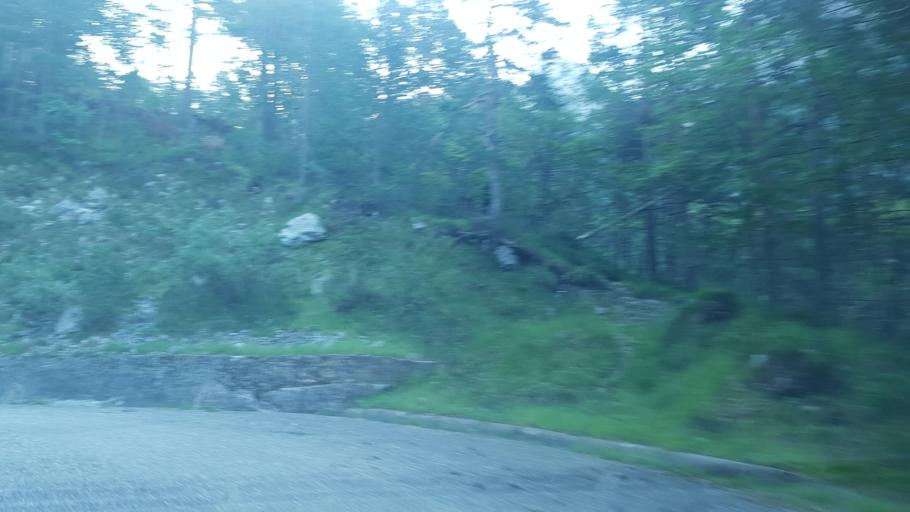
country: IT
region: Friuli Venezia Giulia
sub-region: Provincia di Udine
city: Malborghetto
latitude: 46.4591
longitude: 13.4160
